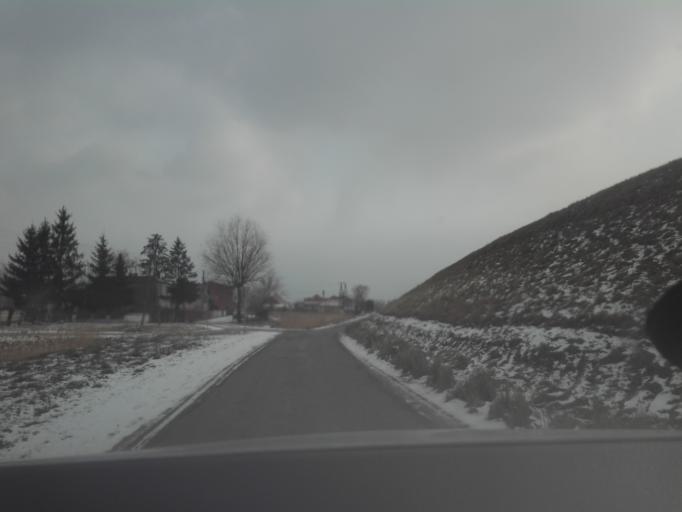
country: PL
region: Subcarpathian Voivodeship
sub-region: Powiat tarnobrzeski
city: Sokolniki
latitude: 50.6526
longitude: 21.7815
